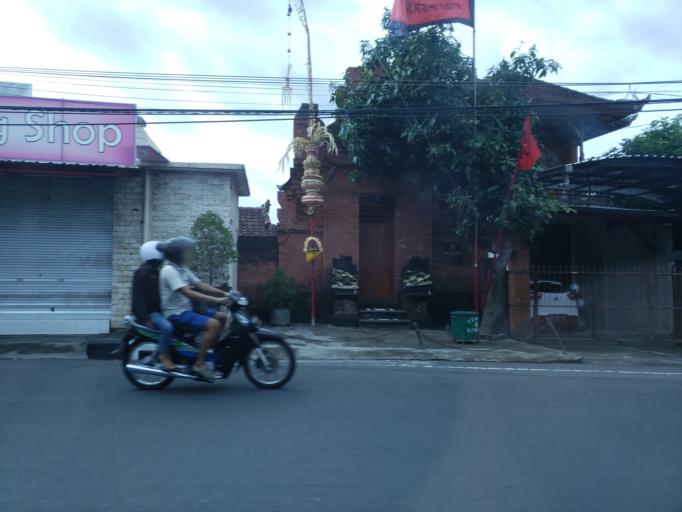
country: ID
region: Bali
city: Dajan Tangluk
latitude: -8.6469
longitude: 115.2432
